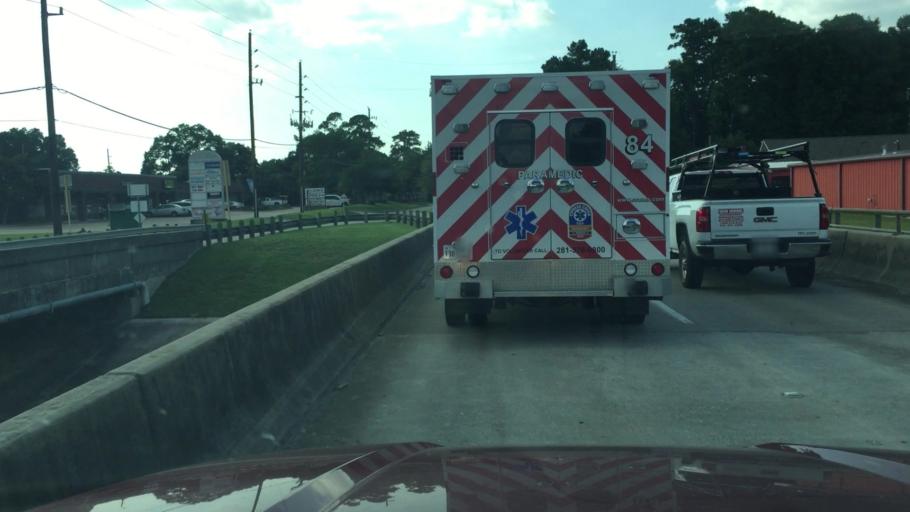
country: US
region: Texas
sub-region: Harris County
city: Tomball
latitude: 30.0283
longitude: -95.5313
